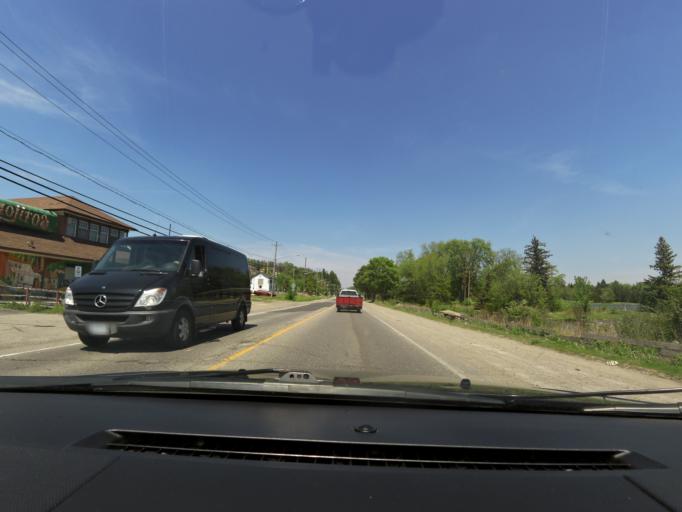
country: CA
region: Ontario
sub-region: Wellington County
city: Guelph
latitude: 43.5569
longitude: -80.2170
